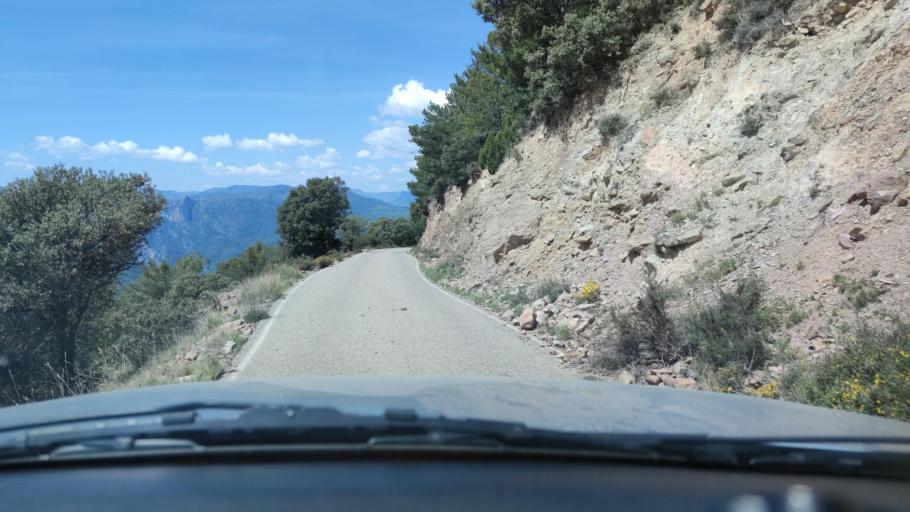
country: ES
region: Catalonia
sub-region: Provincia de Lleida
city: Sort
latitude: 42.3098
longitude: 1.1106
